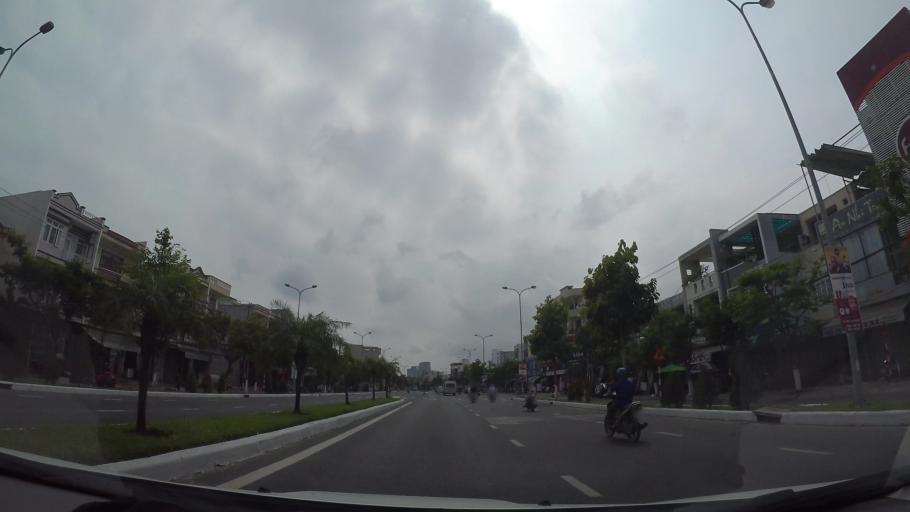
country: VN
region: Da Nang
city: Da Nang
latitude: 16.0791
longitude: 108.2331
